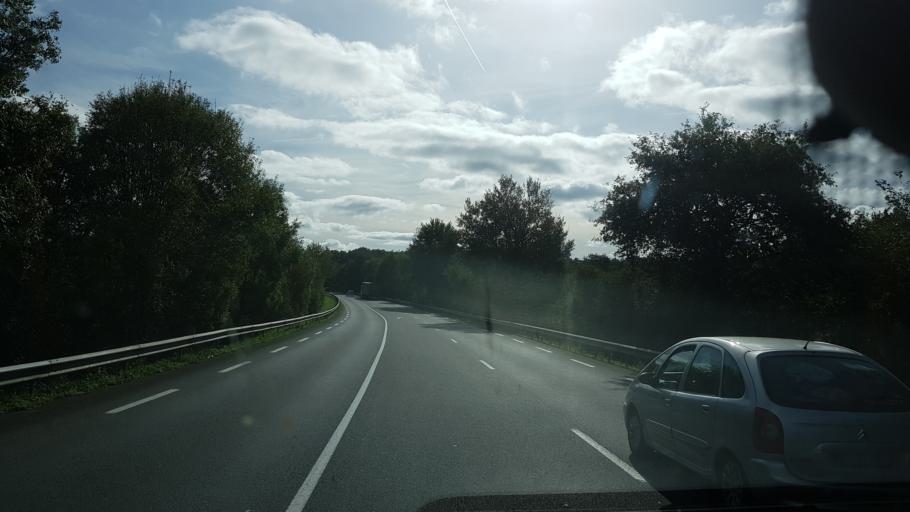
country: FR
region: Poitou-Charentes
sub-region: Departement de la Charente
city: Confolens
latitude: 46.0592
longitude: 0.6666
